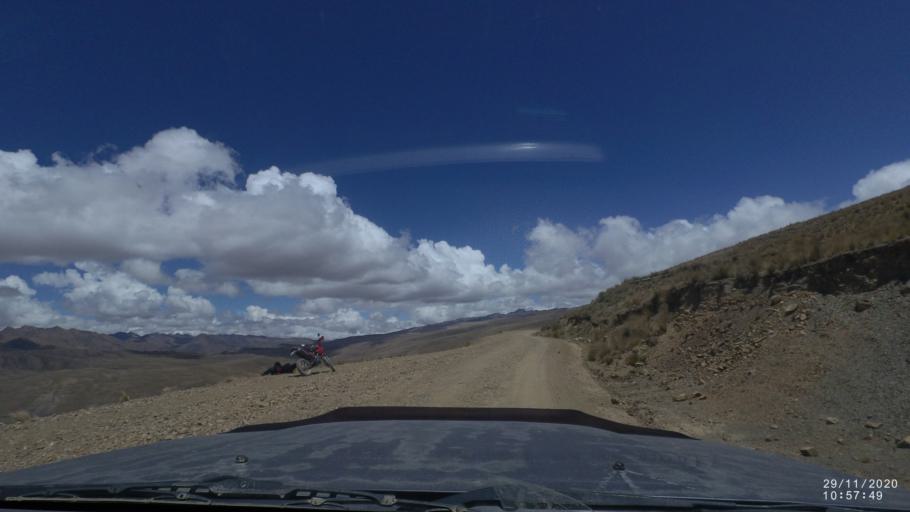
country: BO
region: Cochabamba
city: Cochabamba
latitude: -17.2134
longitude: -66.2316
